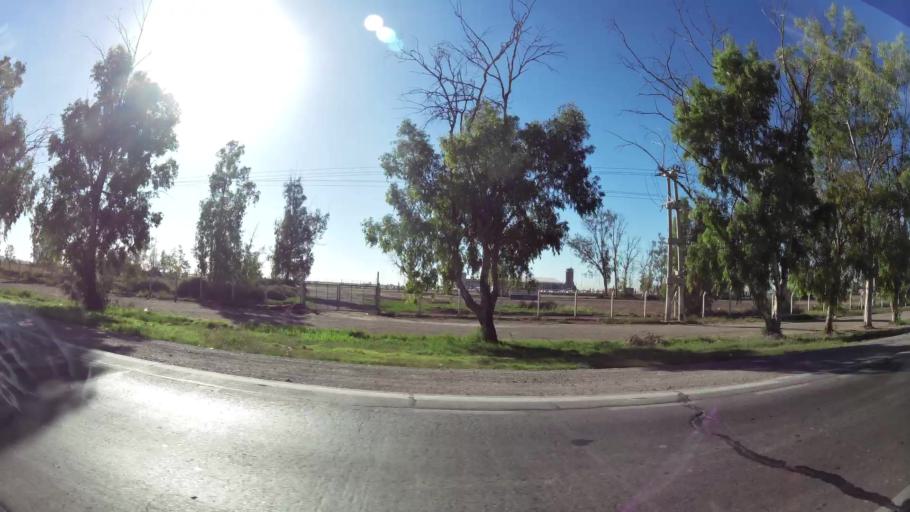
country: AR
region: Mendoza
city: Las Heras
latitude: -32.8254
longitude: -68.8037
